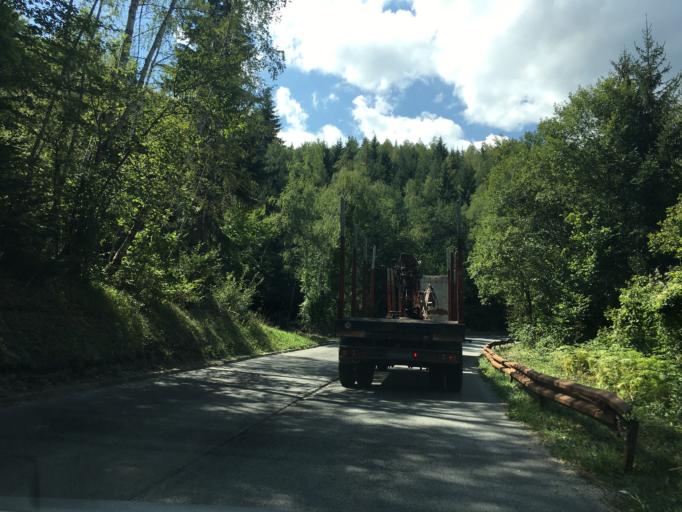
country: RS
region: Central Serbia
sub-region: Zlatiborski Okrug
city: Prijepolje
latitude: 43.3298
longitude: 19.5392
